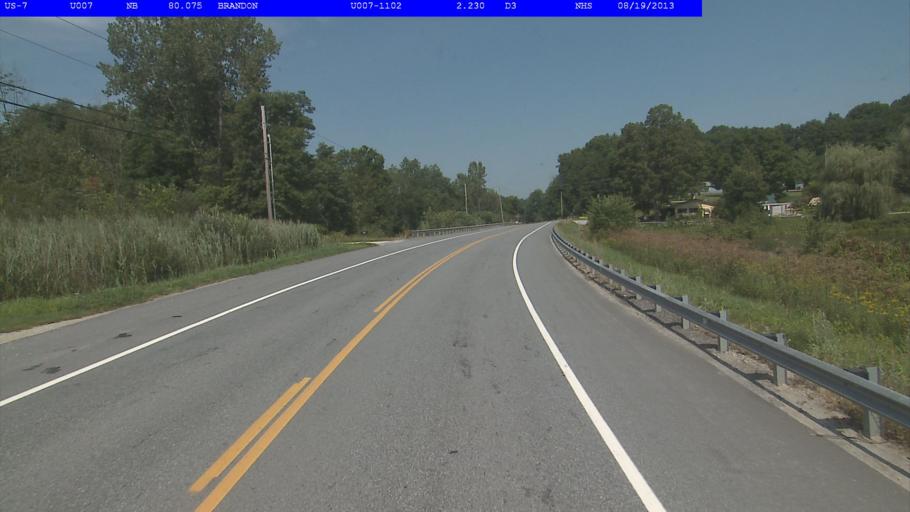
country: US
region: Vermont
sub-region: Rutland County
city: Brandon
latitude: 43.7834
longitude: -73.0634
